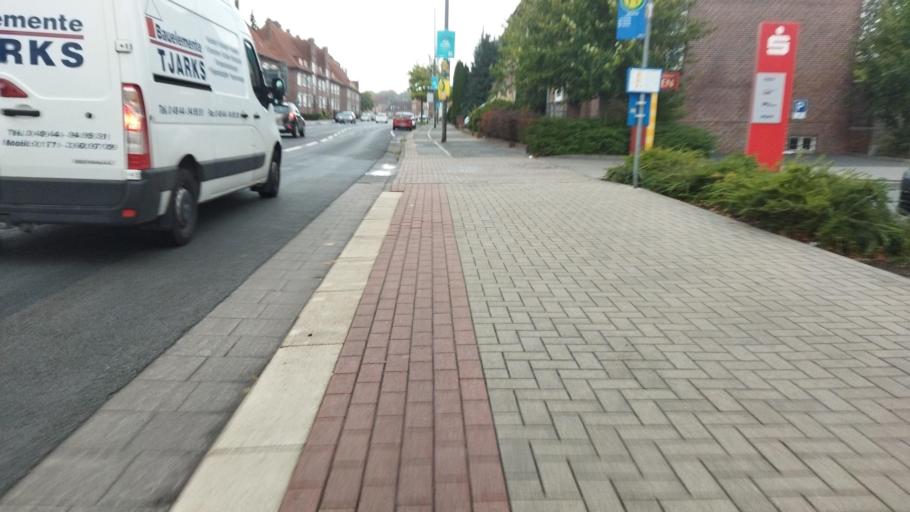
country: DE
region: Lower Saxony
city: Emden
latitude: 53.3805
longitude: 7.2066
